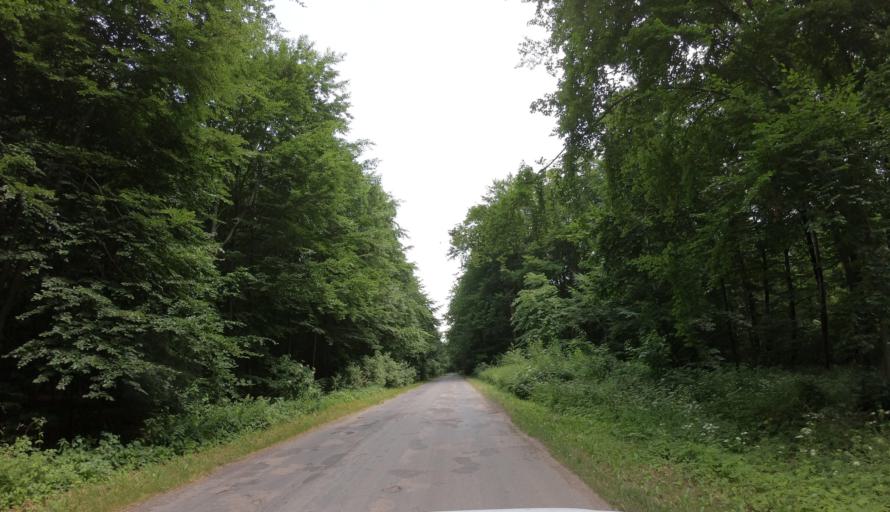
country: PL
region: West Pomeranian Voivodeship
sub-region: Powiat pyrzycki
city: Kozielice
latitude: 53.0690
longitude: 14.7975
